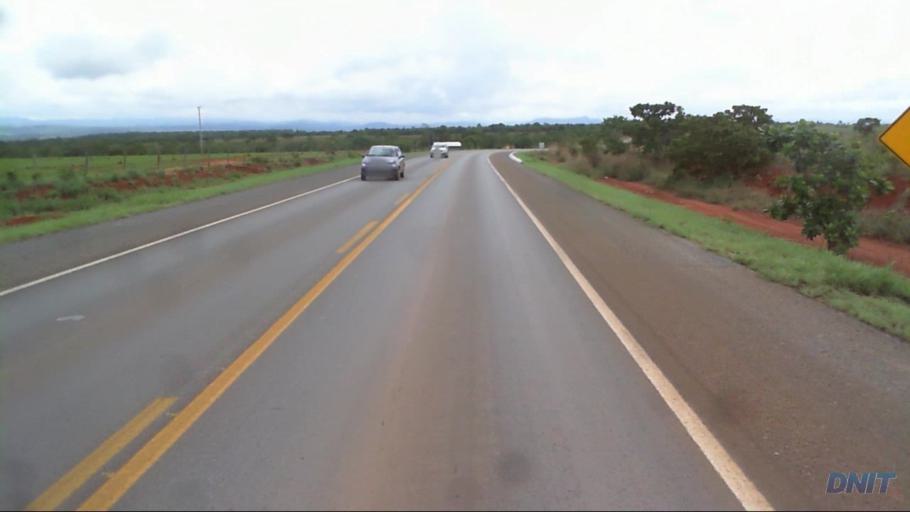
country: BR
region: Goias
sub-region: Padre Bernardo
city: Padre Bernardo
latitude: -15.1578
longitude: -48.3569
